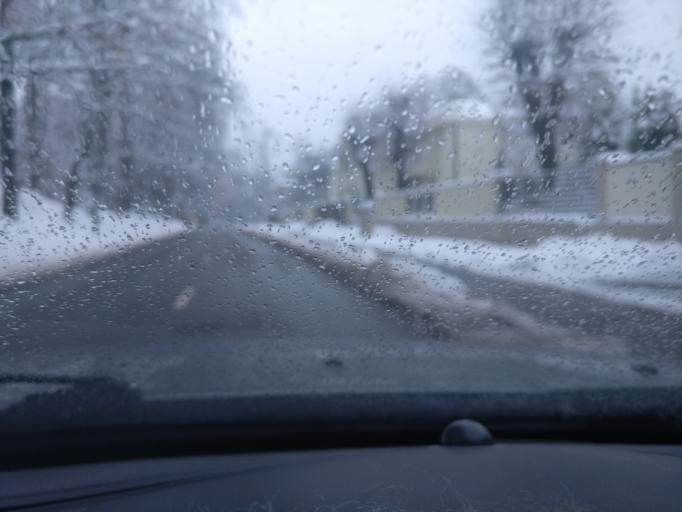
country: LV
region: Riga
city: Riga
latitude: 56.9330
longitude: 24.0801
